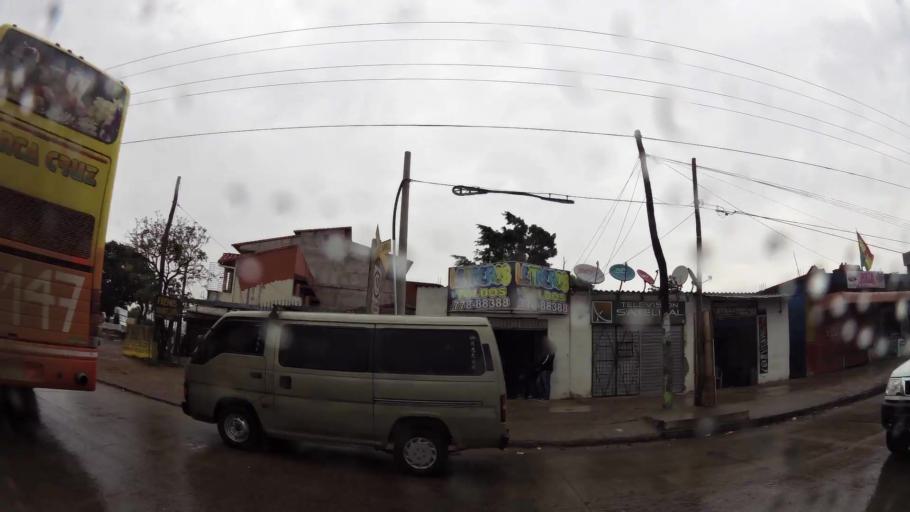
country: BO
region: Santa Cruz
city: Santa Cruz de la Sierra
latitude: -17.8005
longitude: -63.1428
